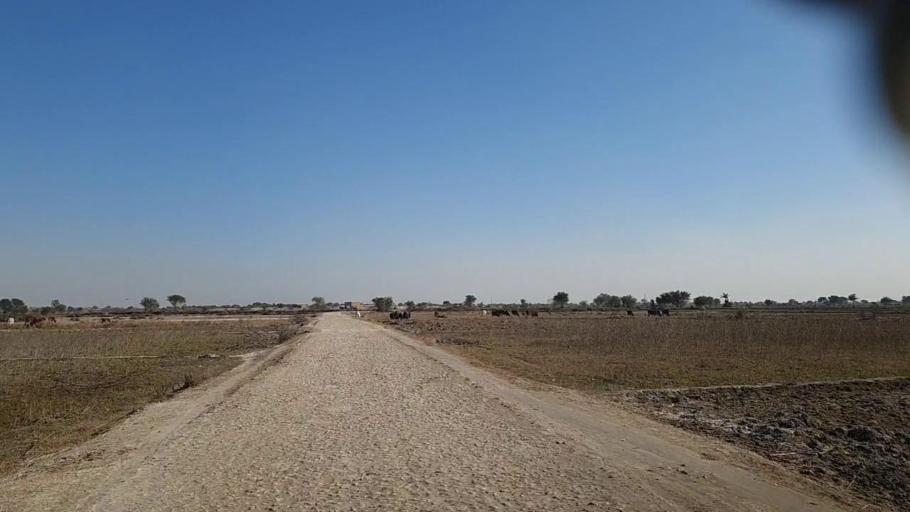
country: PK
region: Sindh
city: Khairpur
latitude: 27.9262
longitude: 69.7346
